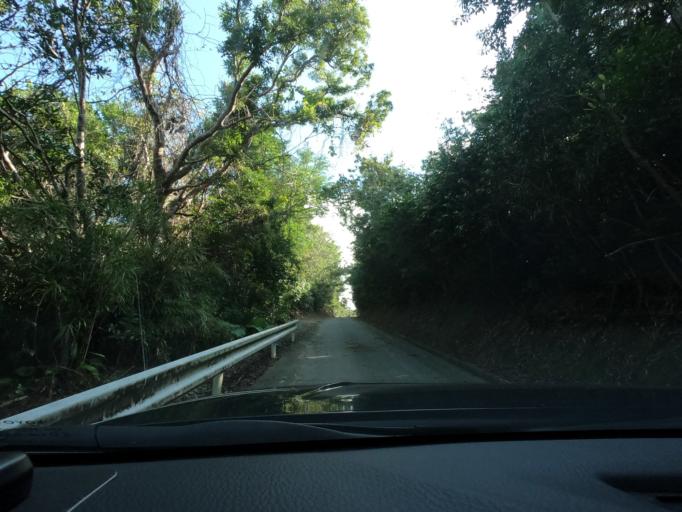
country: JP
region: Okinawa
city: Nago
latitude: 26.7554
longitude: 128.2015
